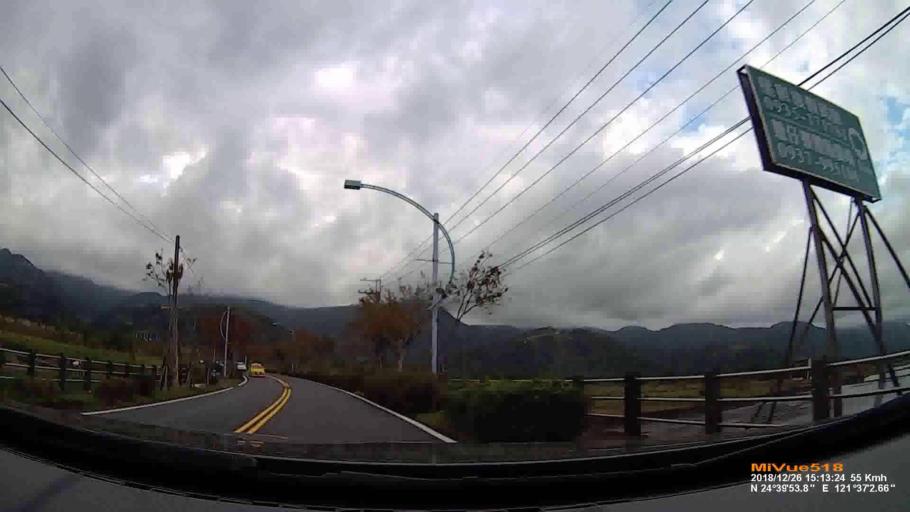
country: TW
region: Taiwan
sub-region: Yilan
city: Yilan
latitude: 24.6672
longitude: 121.5925
